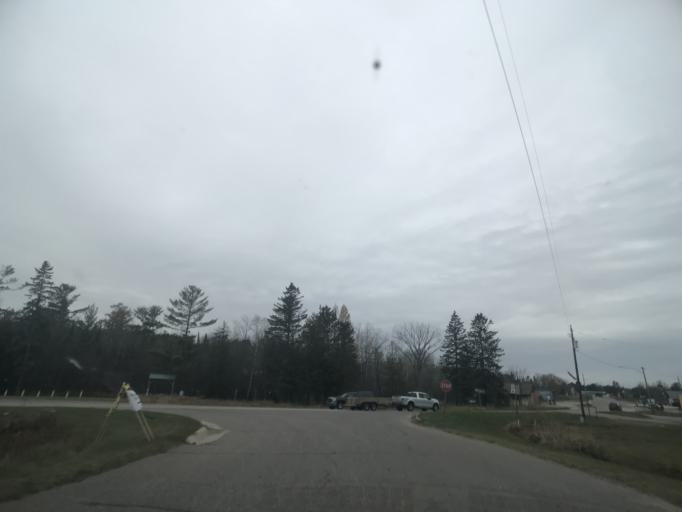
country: US
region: Wisconsin
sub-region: Menominee County
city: Legend Lake
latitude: 45.1829
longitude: -88.4709
